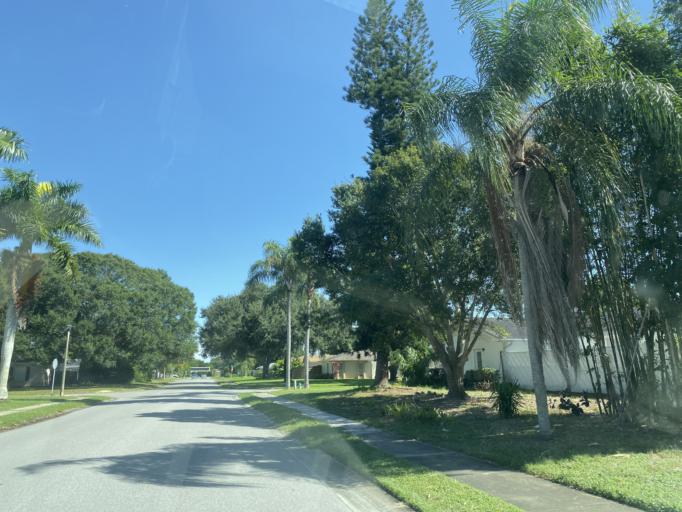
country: US
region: Florida
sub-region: Manatee County
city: West Bradenton
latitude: 27.4811
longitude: -82.6020
